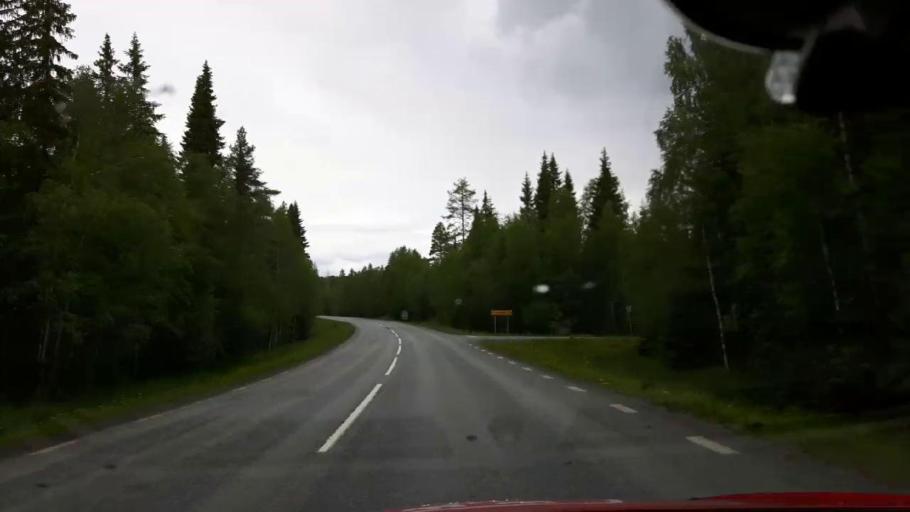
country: SE
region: Jaemtland
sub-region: Krokoms Kommun
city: Krokom
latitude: 63.4325
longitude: 14.2080
